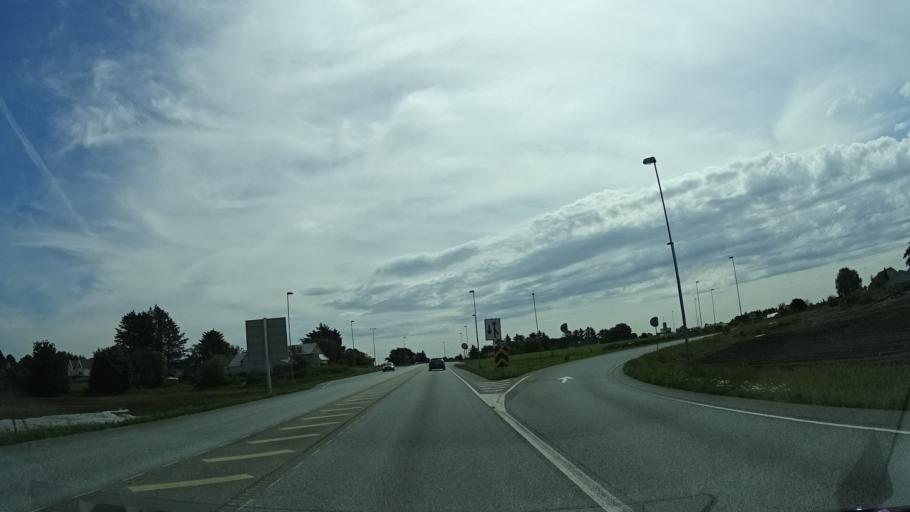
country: NO
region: Rogaland
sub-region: Randaberg
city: Randaberg
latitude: 59.0091
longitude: 5.6388
